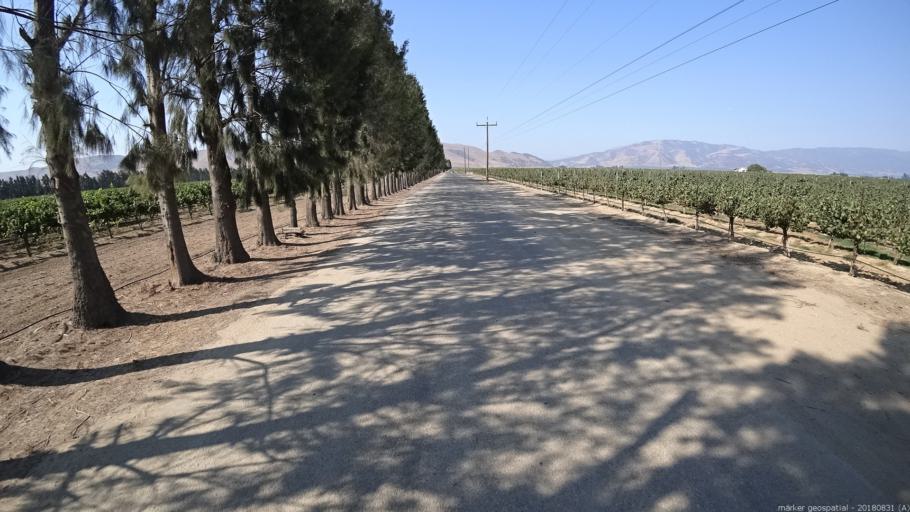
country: US
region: California
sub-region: Monterey County
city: Greenfield
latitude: 36.3015
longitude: -121.2424
